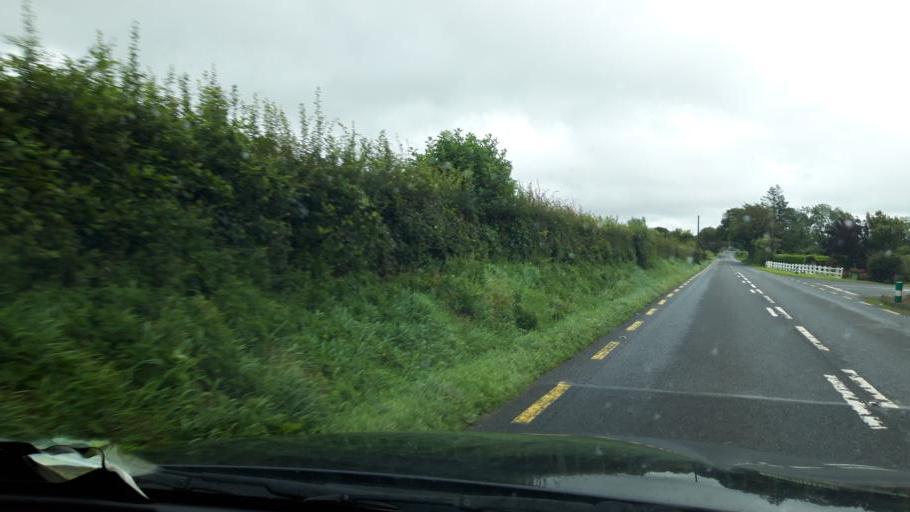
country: IE
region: Leinster
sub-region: Loch Garman
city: New Ross
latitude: 52.4323
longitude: -6.7942
